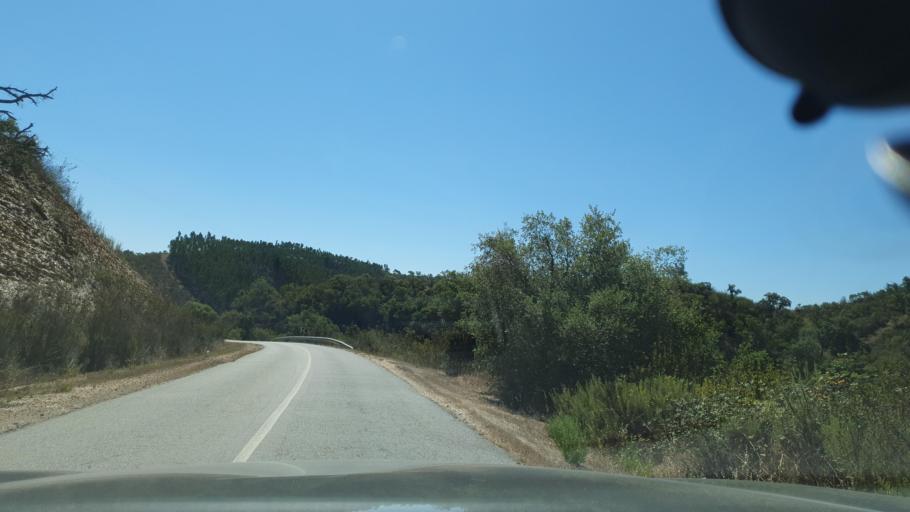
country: PT
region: Beja
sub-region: Odemira
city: Sao Teotonio
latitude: 37.4702
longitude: -8.6123
